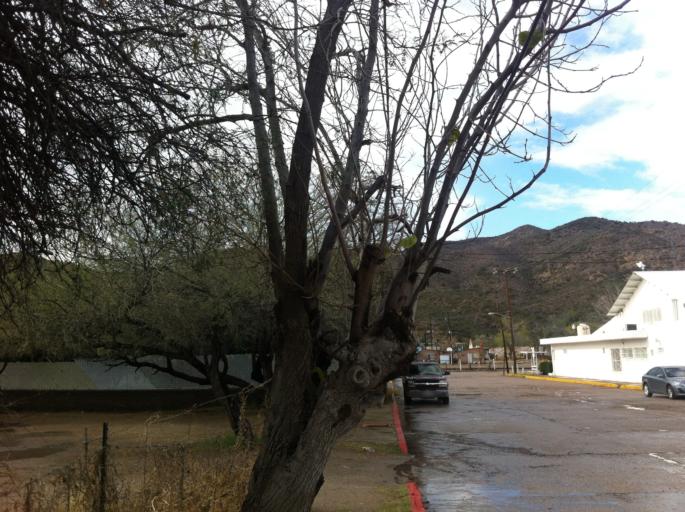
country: MX
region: Sonora
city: Magdalena de Kino
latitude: 30.6376
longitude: -110.9650
